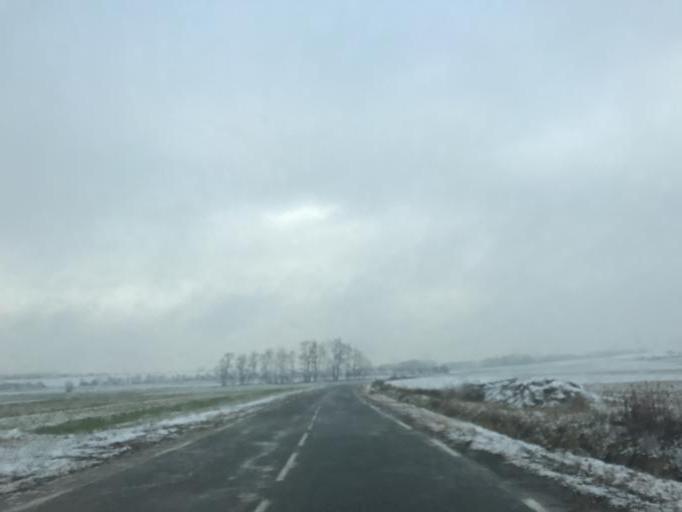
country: FR
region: Rhone-Alpes
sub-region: Departement de l'Ain
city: Miribel
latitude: 45.8415
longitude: 4.9536
